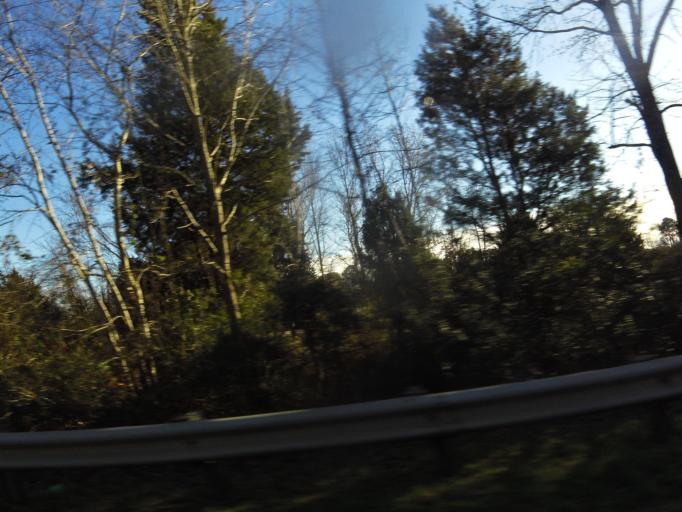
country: US
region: Virginia
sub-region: City of Suffolk
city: Suffolk
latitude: 36.7651
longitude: -76.5549
